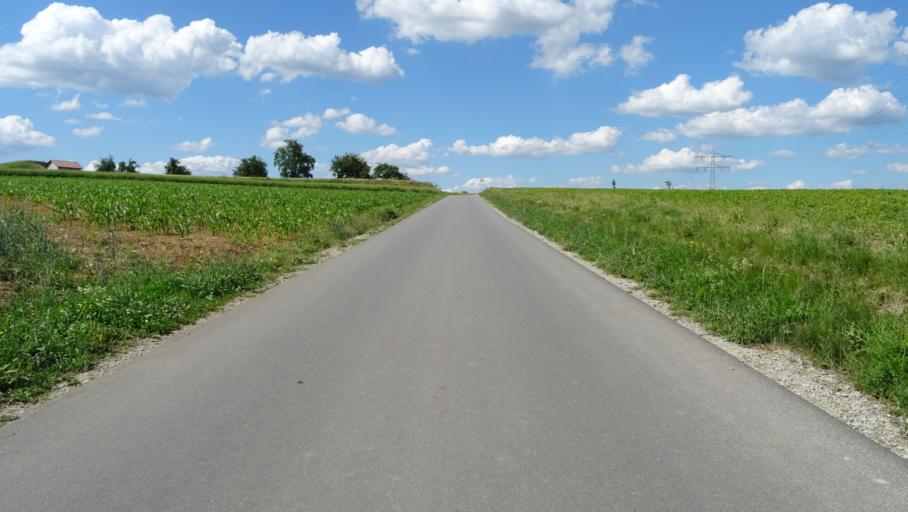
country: DE
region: Baden-Wuerttemberg
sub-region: Karlsruhe Region
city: Adelsheim
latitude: 49.4017
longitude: 9.3666
